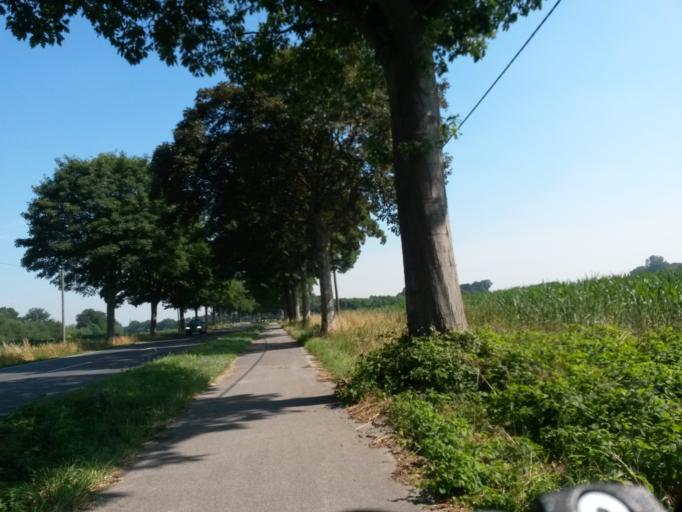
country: DE
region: North Rhine-Westphalia
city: Kempen
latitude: 51.4208
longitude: 6.4183
